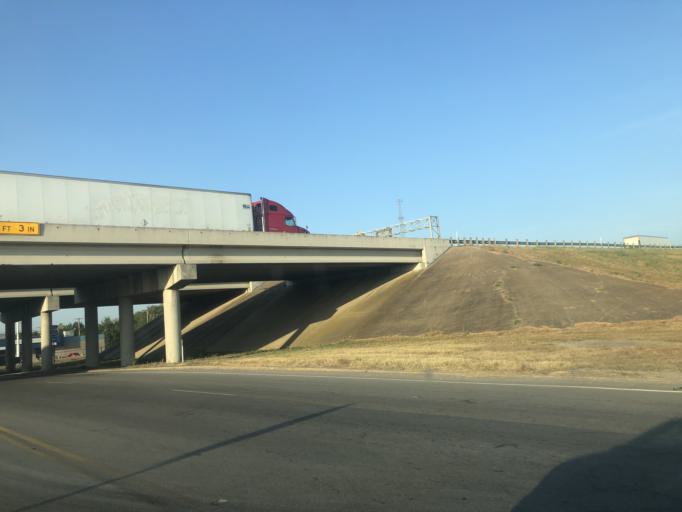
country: US
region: Texas
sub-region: Parker County
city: Aledo
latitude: 32.7214
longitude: -97.5336
